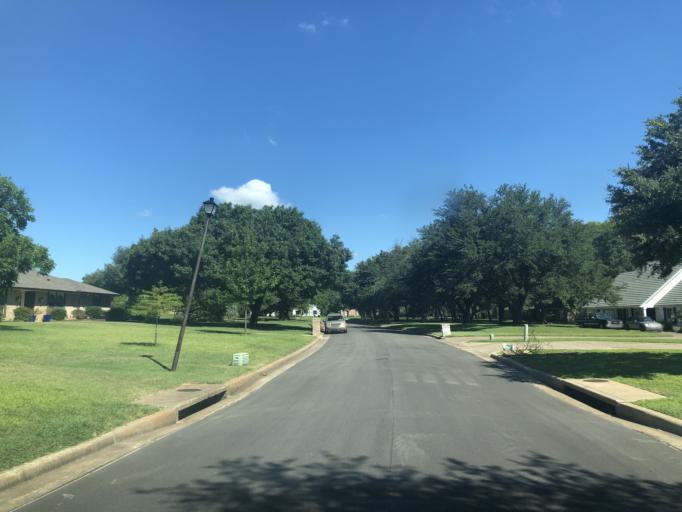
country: US
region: Texas
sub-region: Dallas County
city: Duncanville
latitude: 32.6378
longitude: -96.9383
